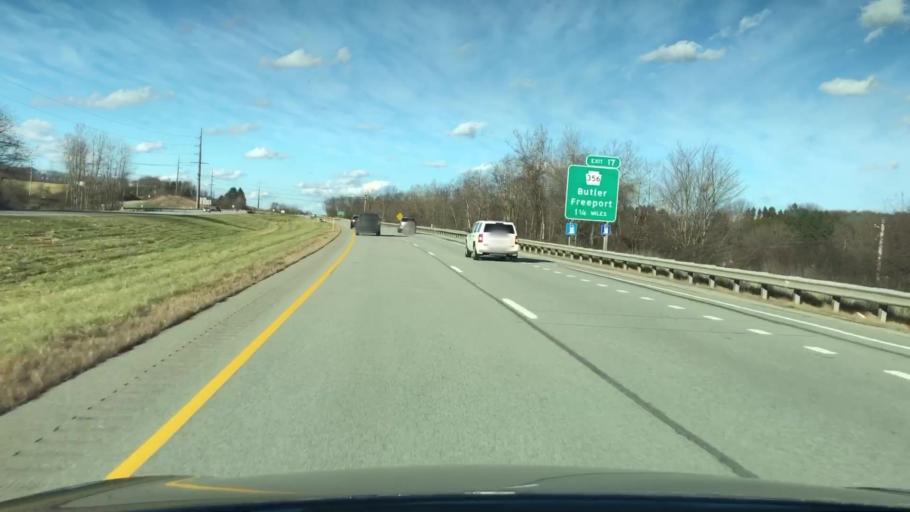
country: US
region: Pennsylvania
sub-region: Armstrong County
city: Freeport
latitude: 40.6734
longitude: -79.7136
